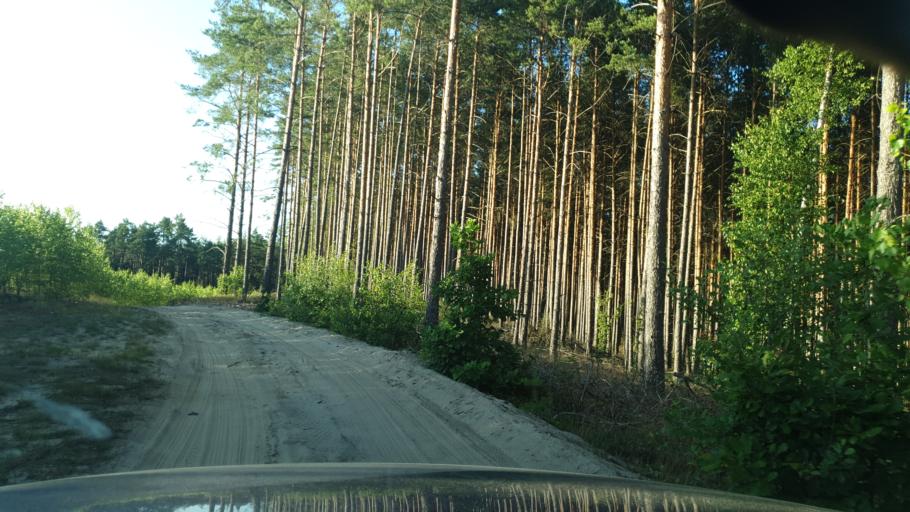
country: PL
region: Pomeranian Voivodeship
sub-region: Powiat bytowski
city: Lipnica
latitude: 53.8837
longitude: 17.4268
